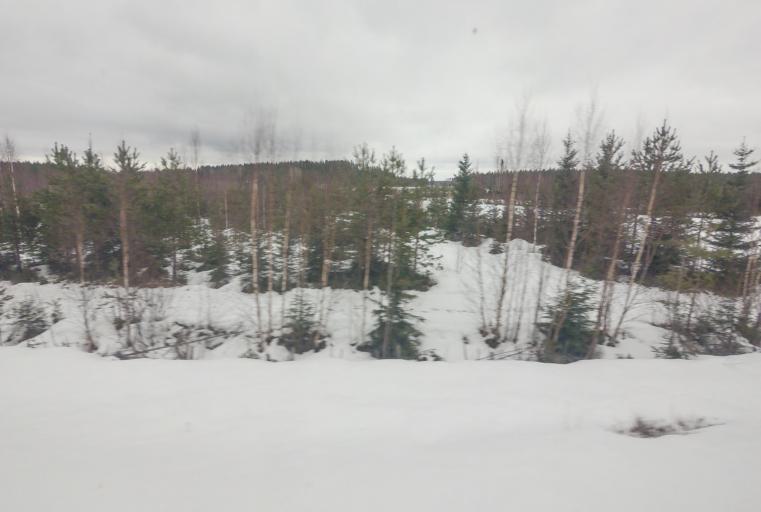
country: FI
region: Southern Savonia
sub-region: Savonlinna
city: Savonlinna
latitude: 61.8690
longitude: 29.0524
